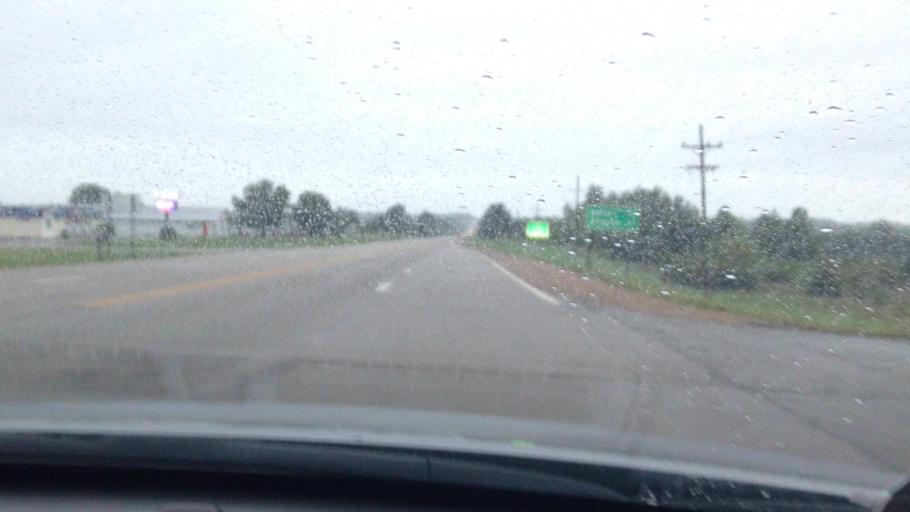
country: US
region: Kansas
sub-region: Brown County
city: Hiawatha
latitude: 39.8392
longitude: -95.5272
